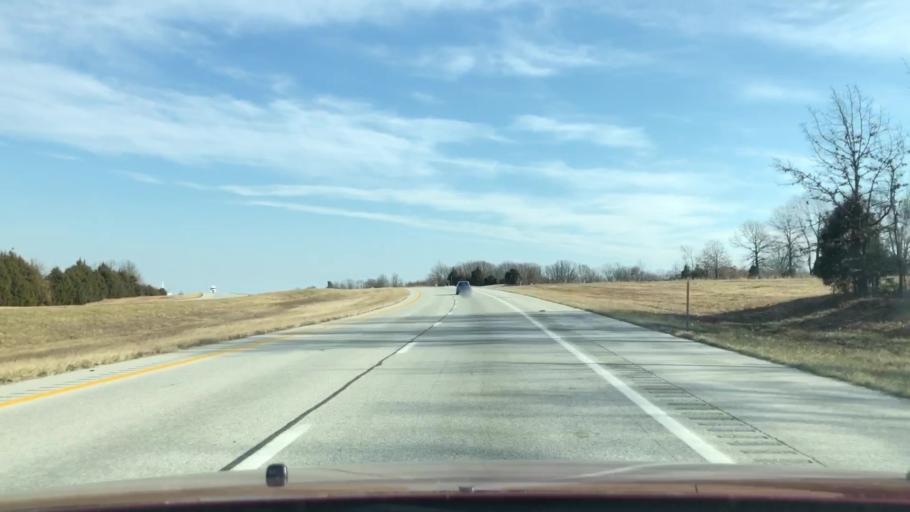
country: US
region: Missouri
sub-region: Webster County
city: Seymour
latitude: 37.1654
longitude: -92.8757
